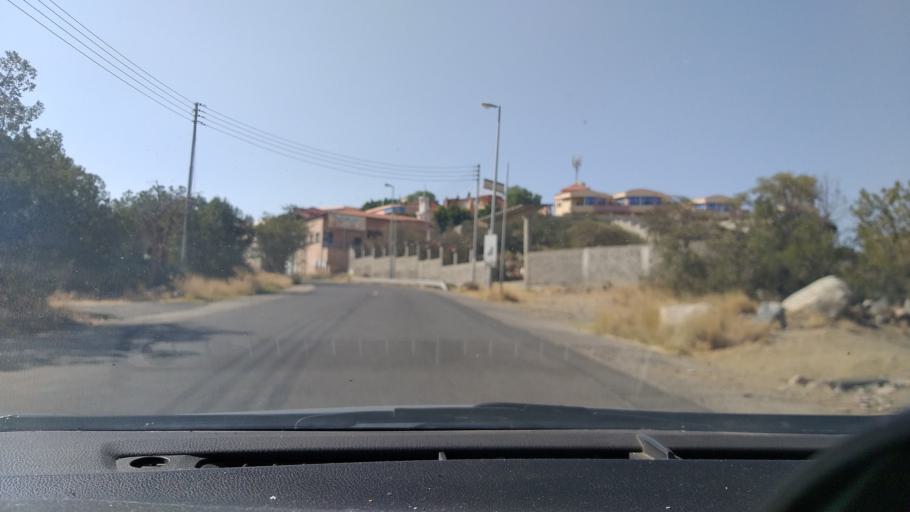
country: SA
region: Makkah
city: Ash Shafa
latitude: 21.0645
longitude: 40.3215
